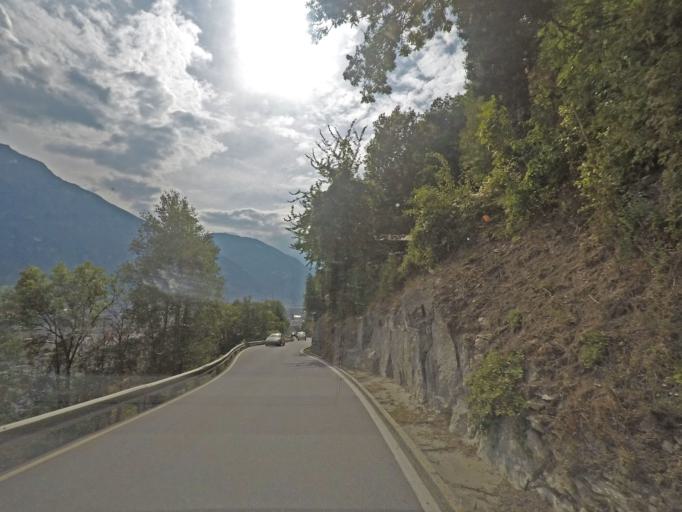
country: CH
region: Valais
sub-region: Brig District
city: Naters
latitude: 46.3309
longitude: 7.9990
